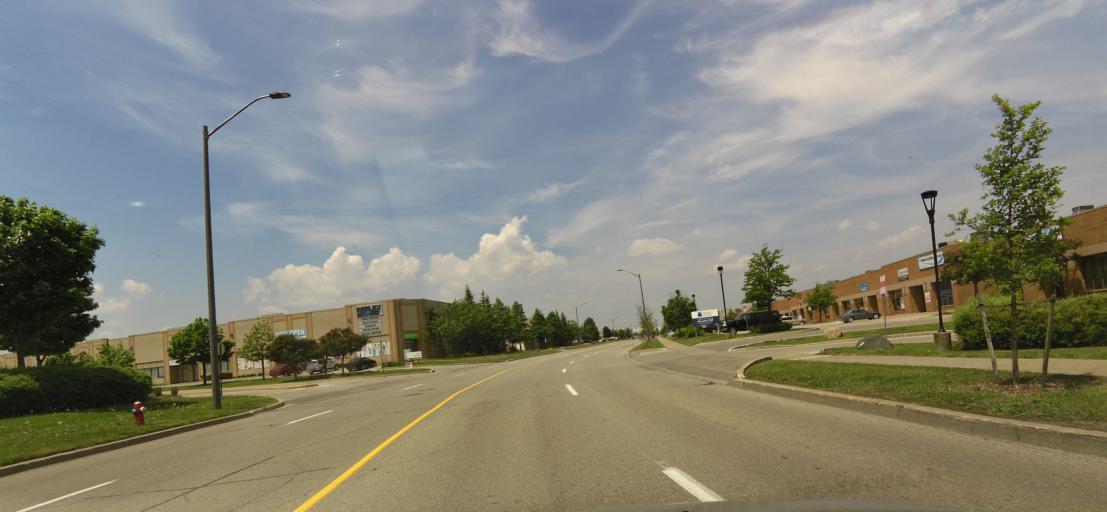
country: CA
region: Ontario
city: Oakville
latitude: 43.5152
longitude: -79.6947
